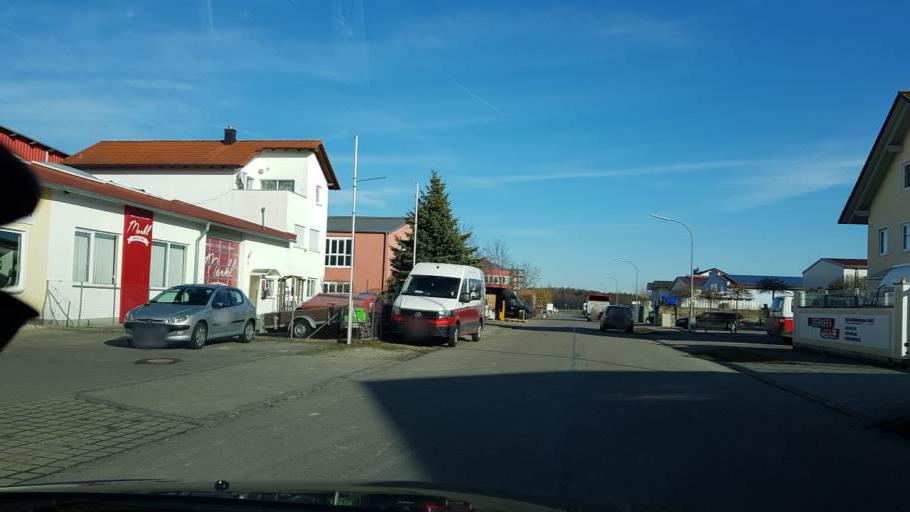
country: DE
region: Bavaria
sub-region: Upper Bavaria
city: Mammendorf
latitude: 48.2149
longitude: 11.1807
